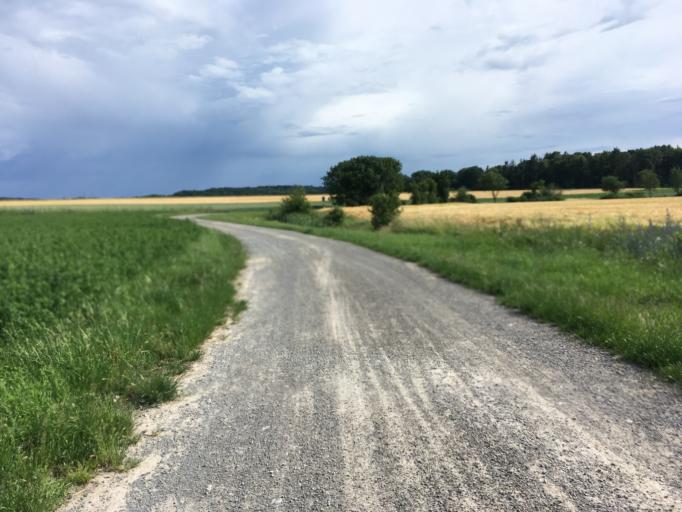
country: DE
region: Baden-Wuerttemberg
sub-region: Regierungsbezirk Stuttgart
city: Oberriexingen
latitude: 48.9461
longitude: 9.0394
